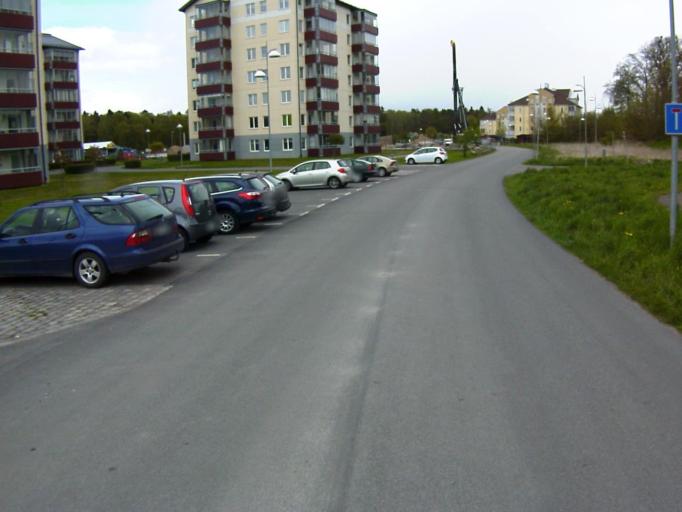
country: SE
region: Skane
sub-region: Kristianstads Kommun
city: Kristianstad
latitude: 56.0437
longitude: 14.1663
